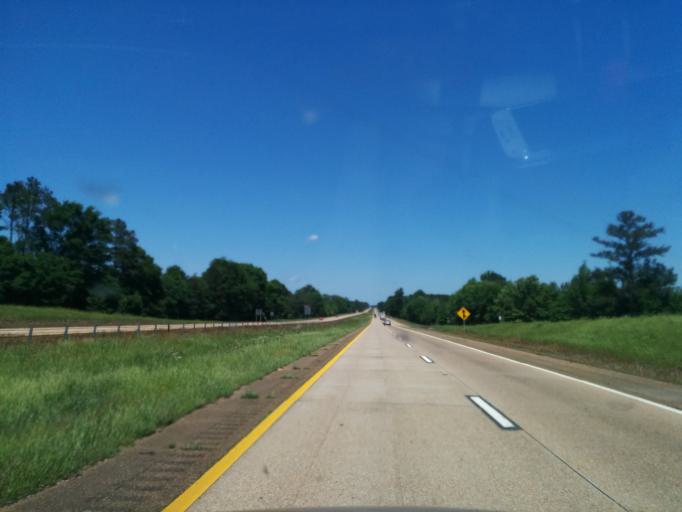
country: US
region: Mississippi
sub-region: Pike County
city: Magnolia
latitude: 31.1116
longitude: -90.4851
